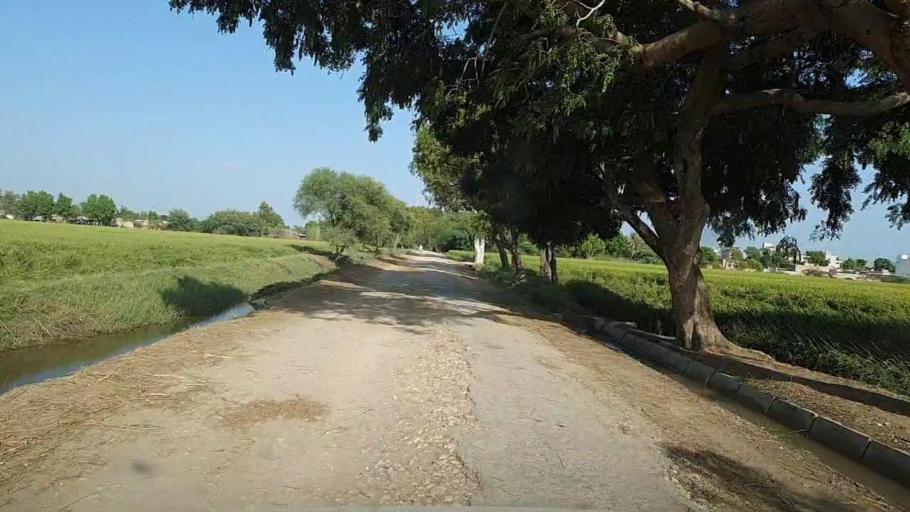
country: PK
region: Sindh
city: Kario
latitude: 24.5996
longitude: 68.5226
